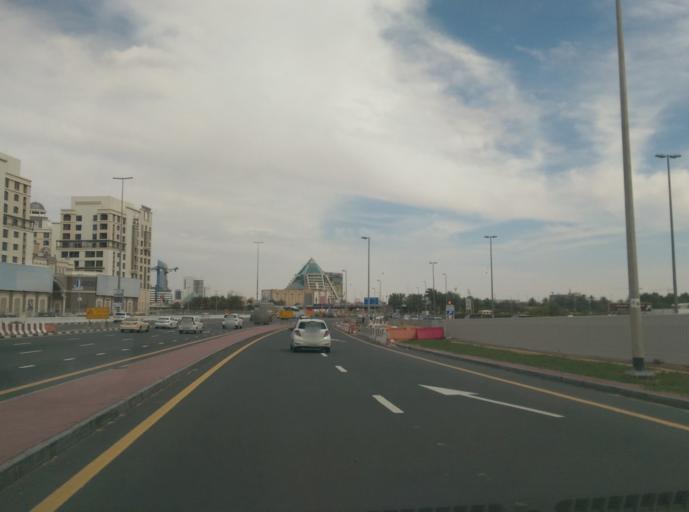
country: AE
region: Ash Shariqah
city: Sharjah
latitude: 25.2315
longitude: 55.3102
